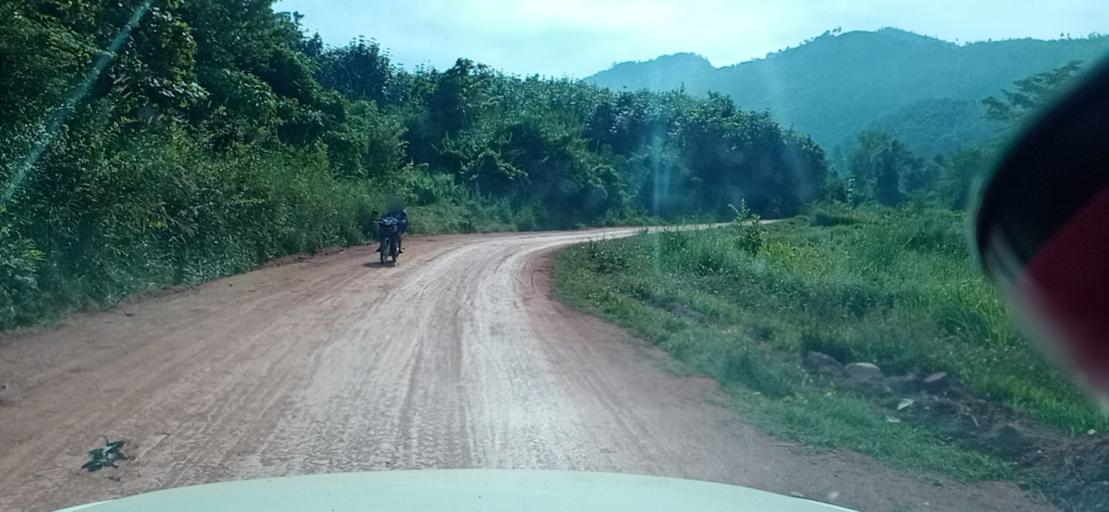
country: TH
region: Changwat Bueng Kan
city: Pak Khat
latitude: 18.6697
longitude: 103.2004
